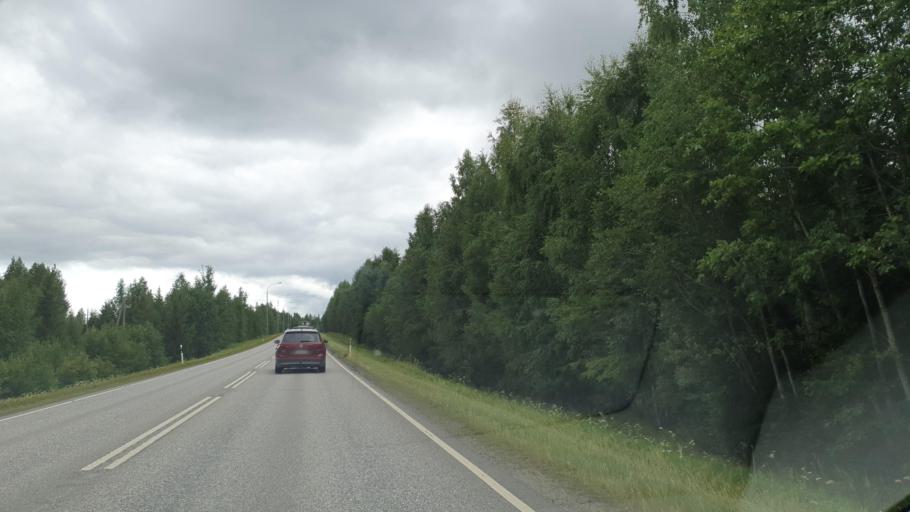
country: FI
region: Northern Savo
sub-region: Ylae-Savo
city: Sonkajaervi
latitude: 63.7017
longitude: 27.3568
